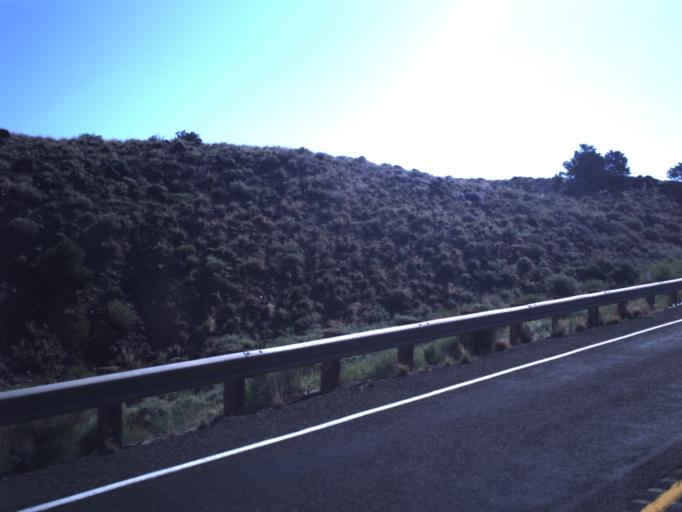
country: US
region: Utah
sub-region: Wayne County
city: Loa
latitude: 38.3040
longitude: -111.4837
